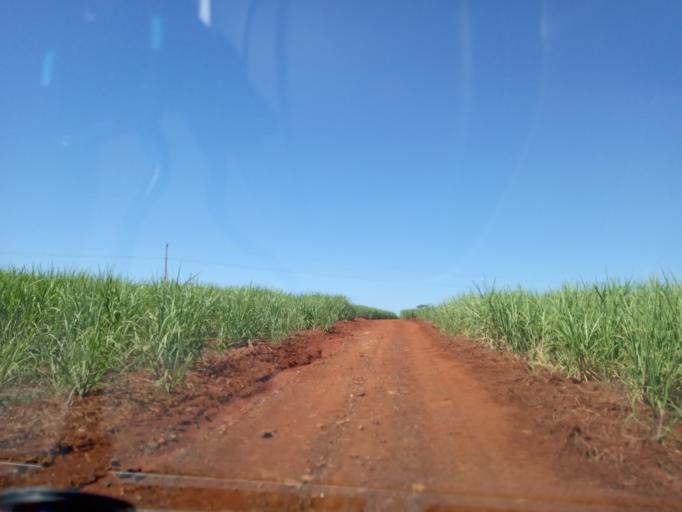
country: BR
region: Goias
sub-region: Itumbiara
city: Itumbiara
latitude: -18.4239
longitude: -49.1671
